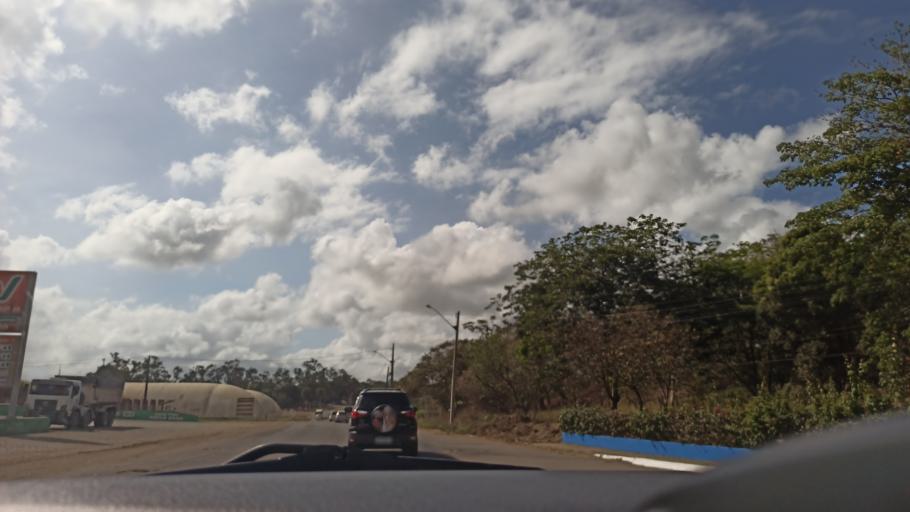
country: BR
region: Paraiba
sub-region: Juripiranga
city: Juripiranga
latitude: -7.4158
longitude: -35.2612
